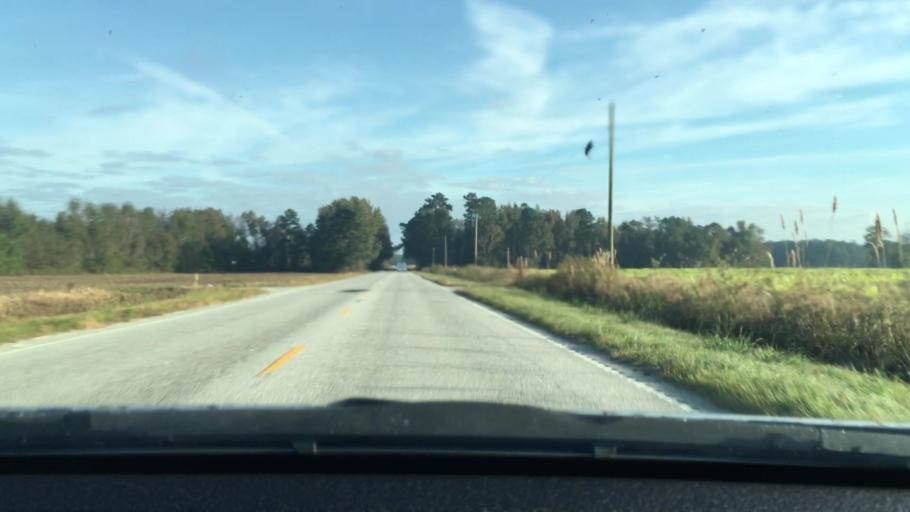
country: US
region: South Carolina
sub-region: Sumter County
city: East Sumter
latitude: 34.0196
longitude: -80.2798
